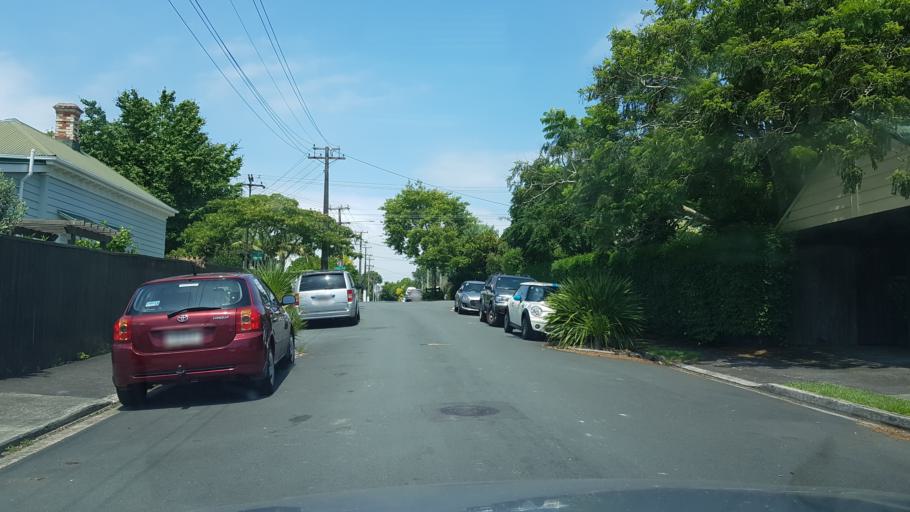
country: NZ
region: Auckland
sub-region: Auckland
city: Auckland
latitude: -36.8238
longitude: 174.8001
